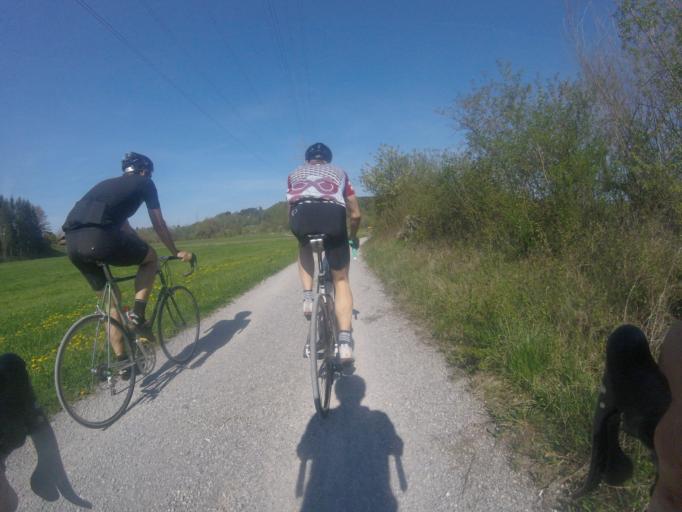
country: CH
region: Bern
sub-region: Bern-Mittelland District
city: Muhleberg
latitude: 46.9746
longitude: 7.2566
